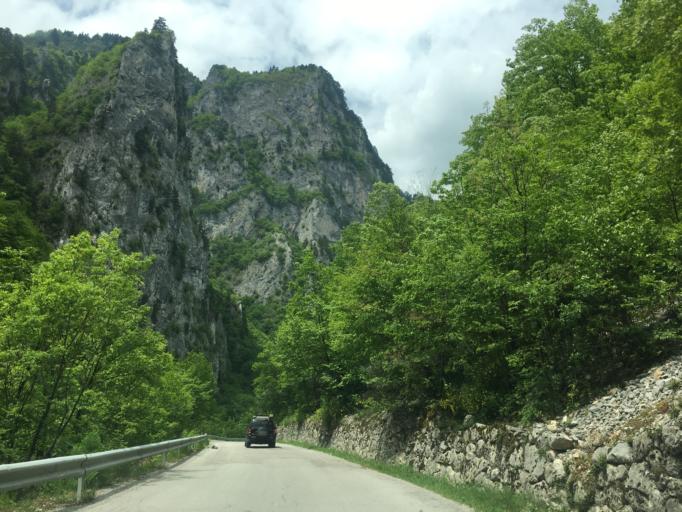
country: XK
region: Pec
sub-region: Komuna e Pejes
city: Peje
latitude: 42.6630
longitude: 20.2117
